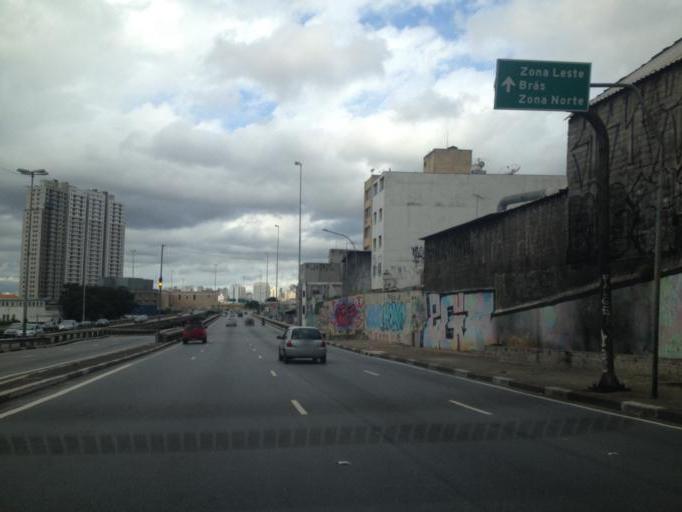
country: BR
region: Sao Paulo
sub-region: Sao Paulo
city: Sao Paulo
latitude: -23.5566
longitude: -46.6325
